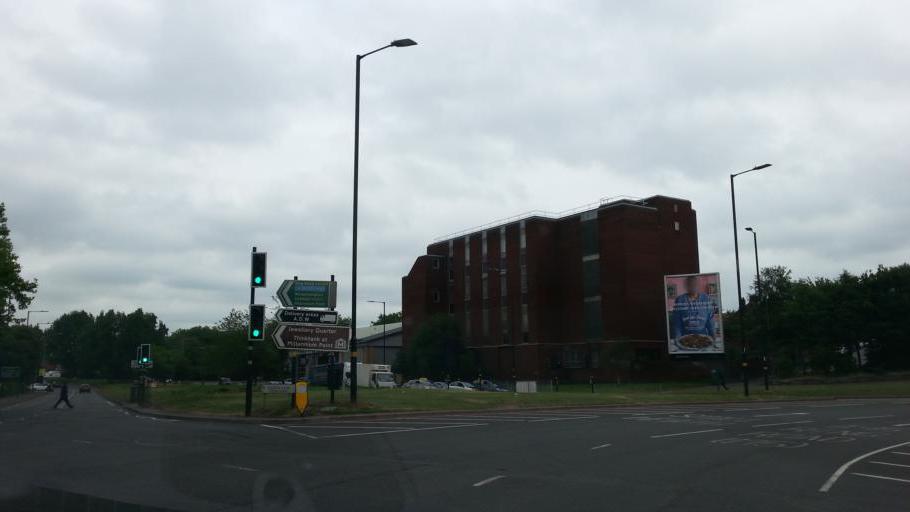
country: GB
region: England
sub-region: City and Borough of Birmingham
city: Birmingham
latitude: 52.4733
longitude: -1.8753
